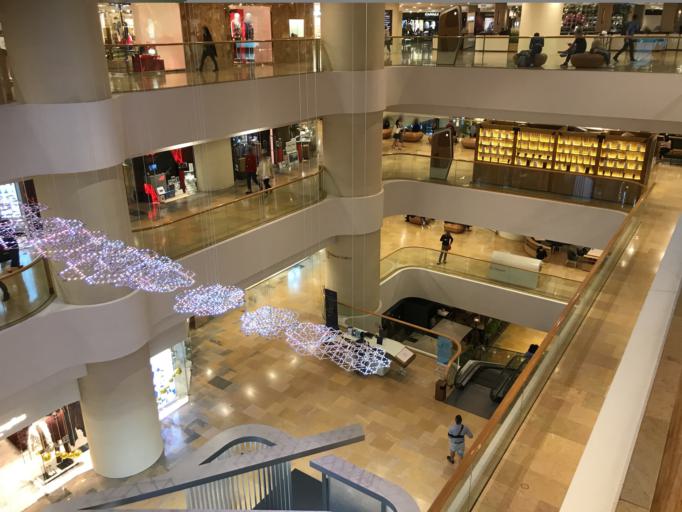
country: HK
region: Wanchai
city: Wan Chai
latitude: 22.2773
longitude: 114.1656
